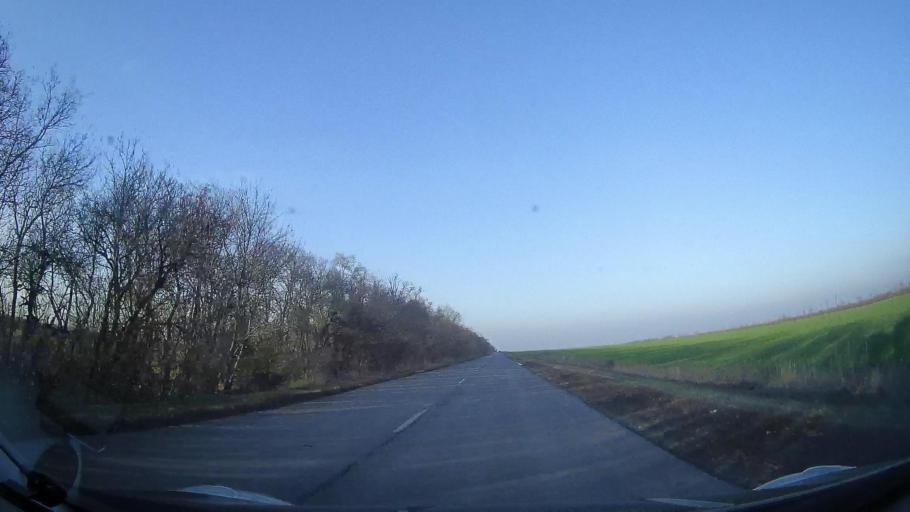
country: RU
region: Rostov
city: Kirovskaya
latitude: 47.0048
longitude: 39.9790
